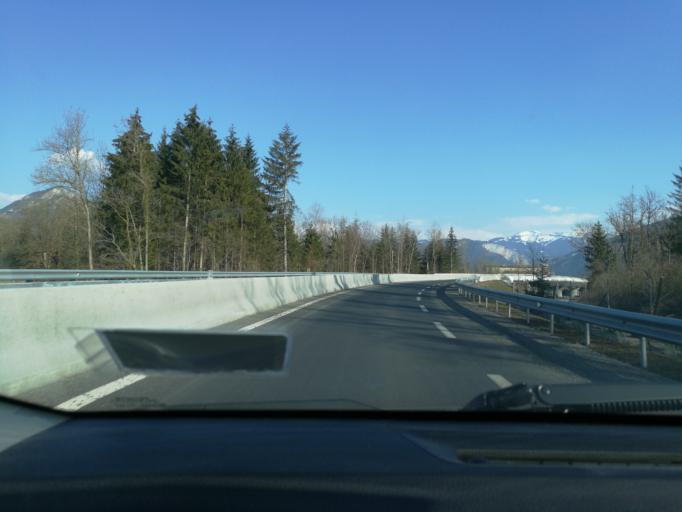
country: FR
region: Rhone-Alpes
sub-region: Departement de la Haute-Savoie
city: Vougy
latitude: 46.0730
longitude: 6.4866
